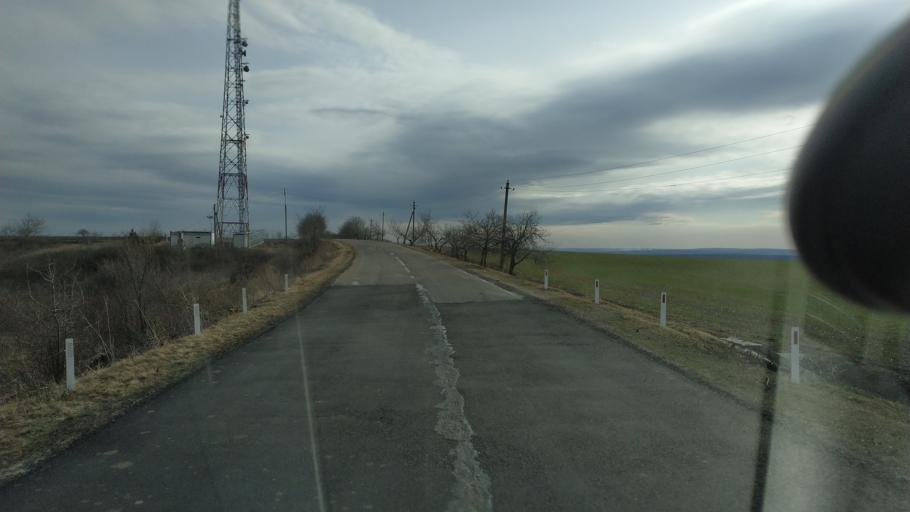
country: MD
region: Telenesti
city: Cocieri
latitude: 47.3622
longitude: 29.0428
